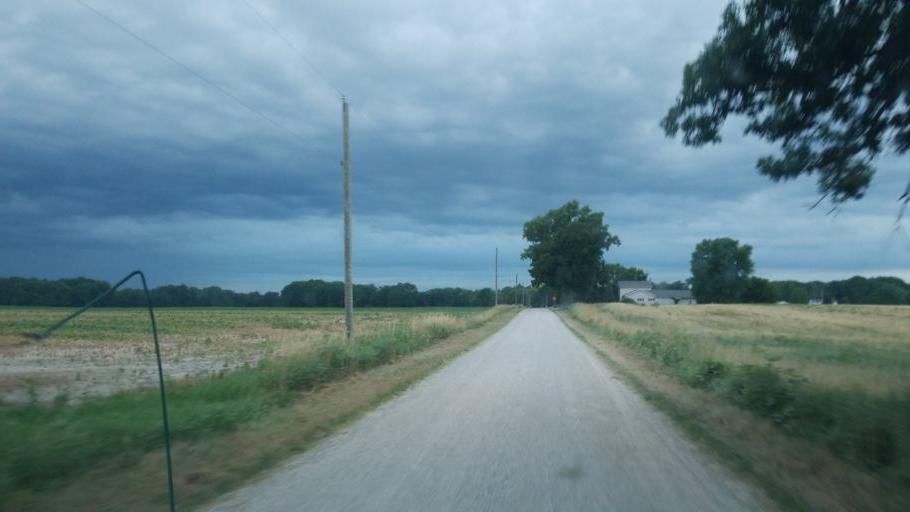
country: US
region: Ohio
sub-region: Defiance County
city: Hicksville
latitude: 41.3282
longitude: -84.8442
